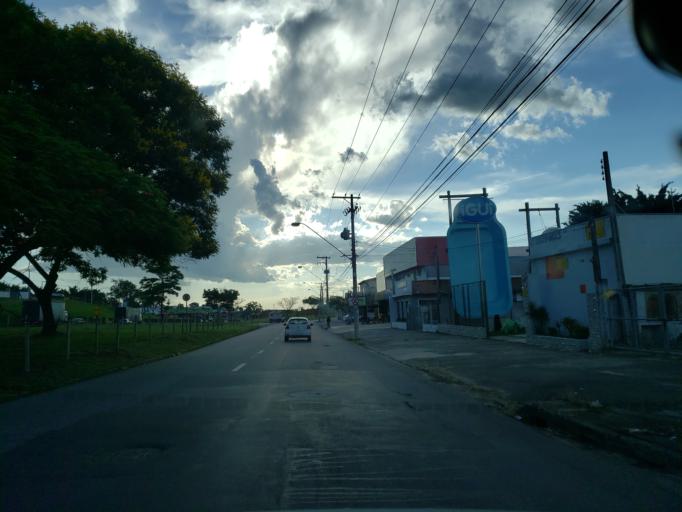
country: BR
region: Sao Paulo
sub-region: Taubate
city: Taubate
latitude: -23.0433
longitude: -45.5794
